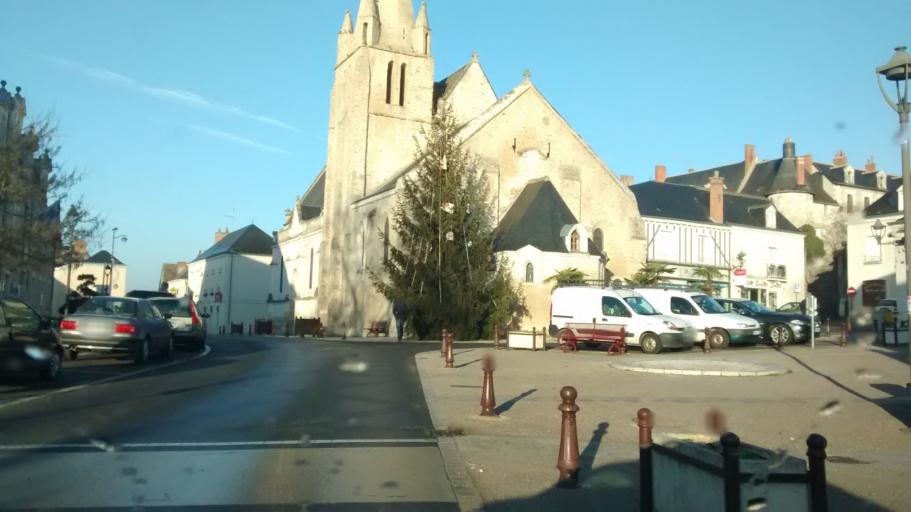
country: FR
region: Centre
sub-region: Departement d'Indre-et-Loire
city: Esvres
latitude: 47.2838
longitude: 0.7859
